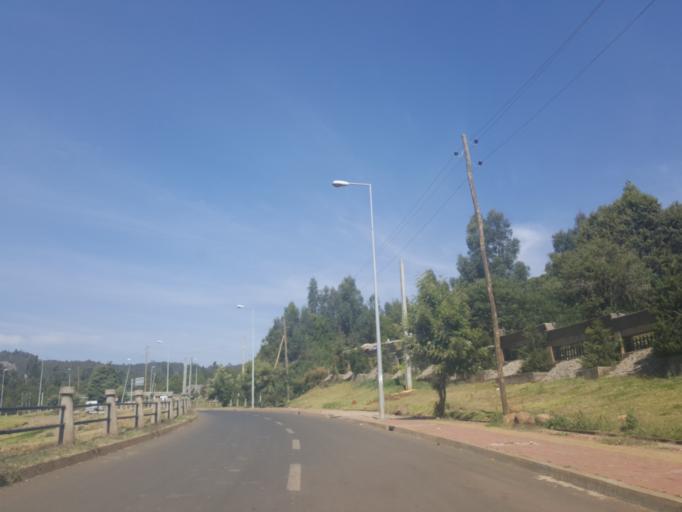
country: ET
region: Adis Abeba
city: Addis Ababa
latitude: 9.0699
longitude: 38.7229
